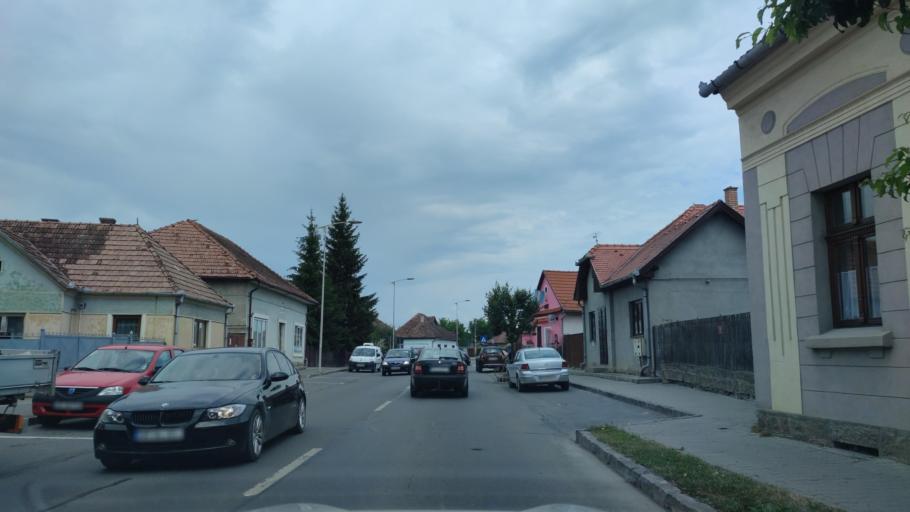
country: RO
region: Harghita
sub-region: Municipiul Miercurea Ciuc
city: Miercurea-Ciuc
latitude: 46.3763
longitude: 25.8011
